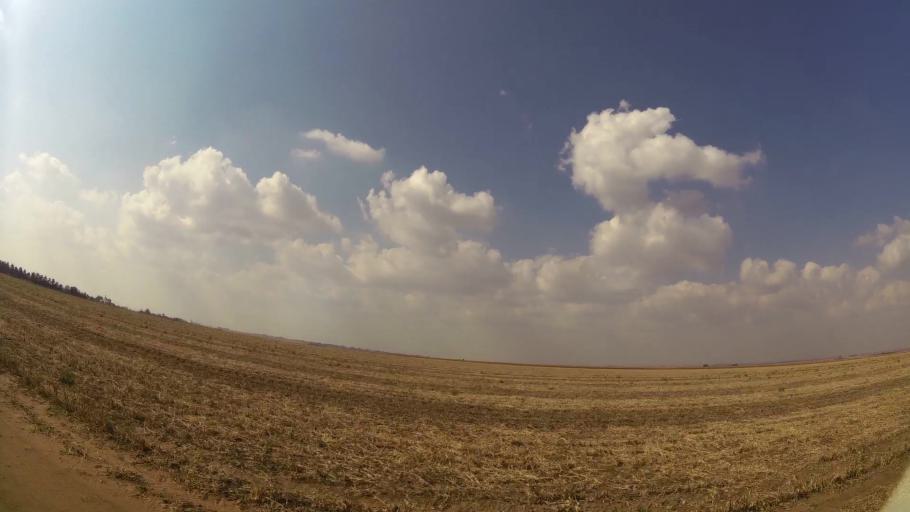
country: ZA
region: Mpumalanga
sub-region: Nkangala District Municipality
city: Delmas
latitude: -26.1939
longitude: 28.5476
